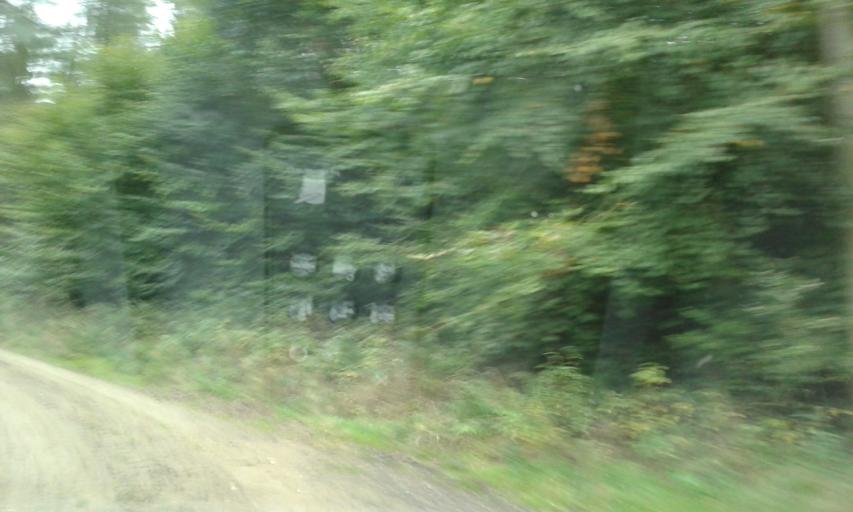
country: PL
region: West Pomeranian Voivodeship
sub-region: Powiat choszczenski
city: Pelczyce
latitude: 53.0849
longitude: 15.2525
